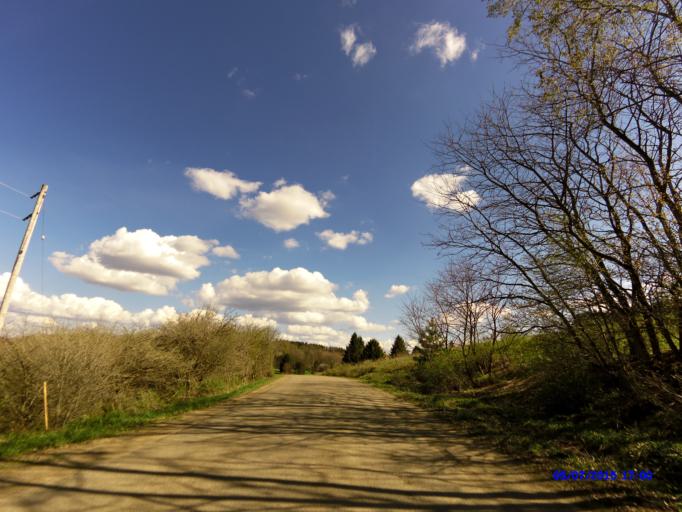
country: US
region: New York
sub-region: Cattaraugus County
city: Little Valley
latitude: 42.2811
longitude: -78.7259
